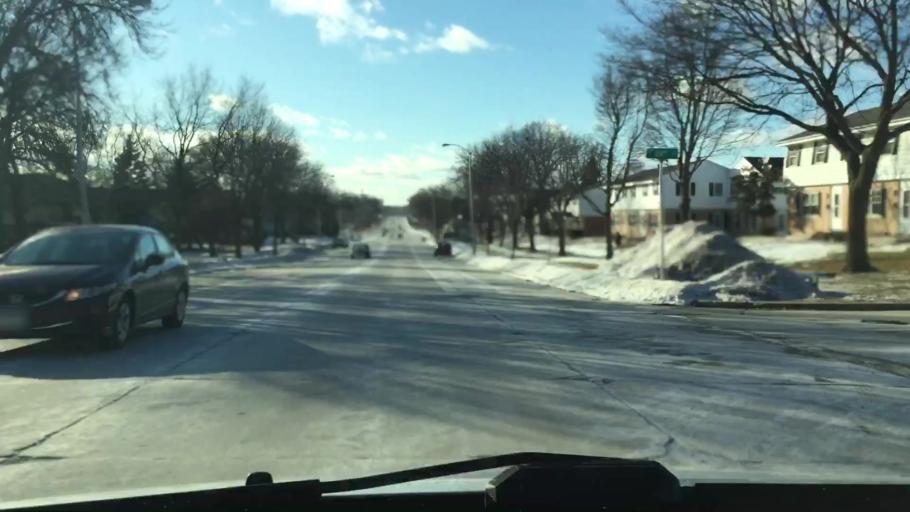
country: US
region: Wisconsin
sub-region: Milwaukee County
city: Greenfield
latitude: 42.9737
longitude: -88.0240
